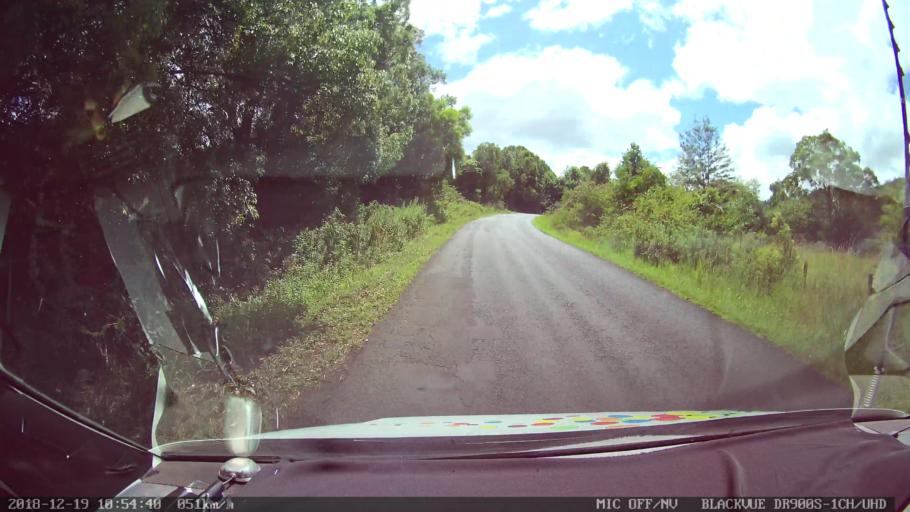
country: AU
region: New South Wales
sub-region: Lismore Municipality
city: Nimbin
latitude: -28.5941
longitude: 153.2475
